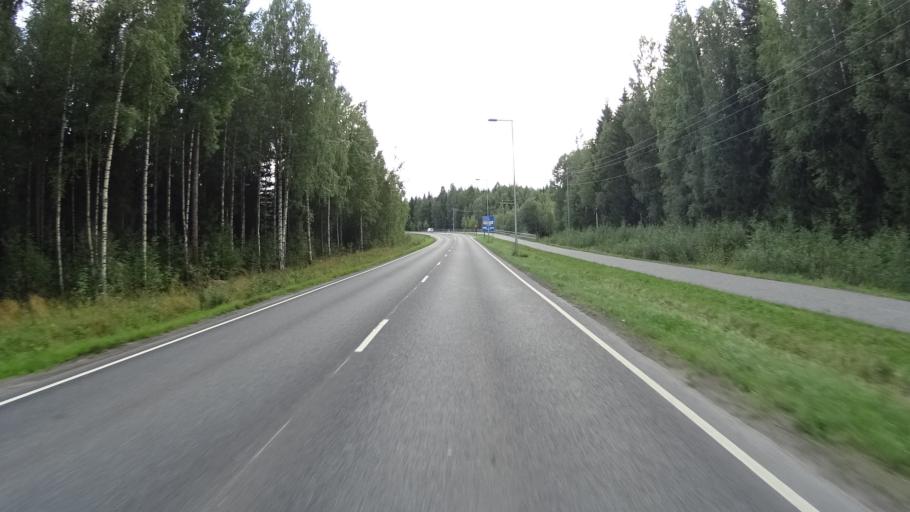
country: FI
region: Uusimaa
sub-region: Helsinki
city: Kilo
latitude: 60.3153
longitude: 24.8603
